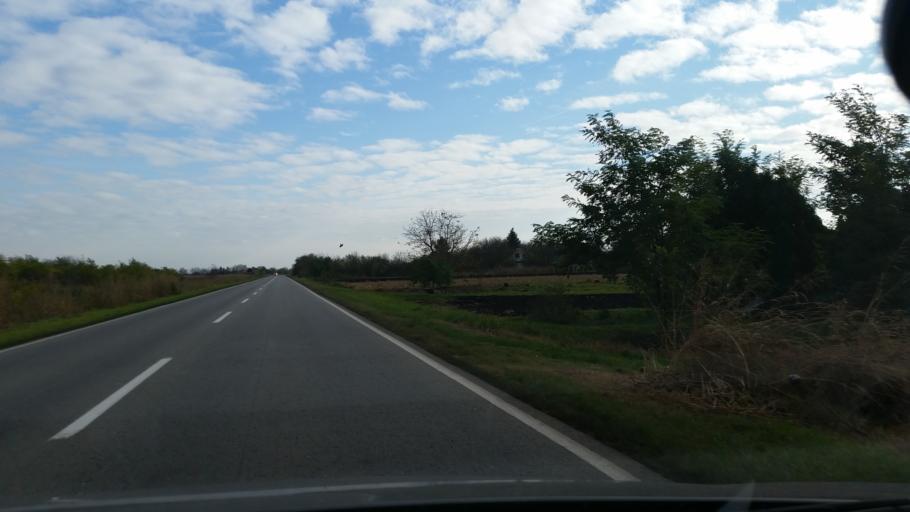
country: RS
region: Autonomna Pokrajina Vojvodina
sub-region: Srednjebanatski Okrug
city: Zrenjanin
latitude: 45.4401
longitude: 20.3633
